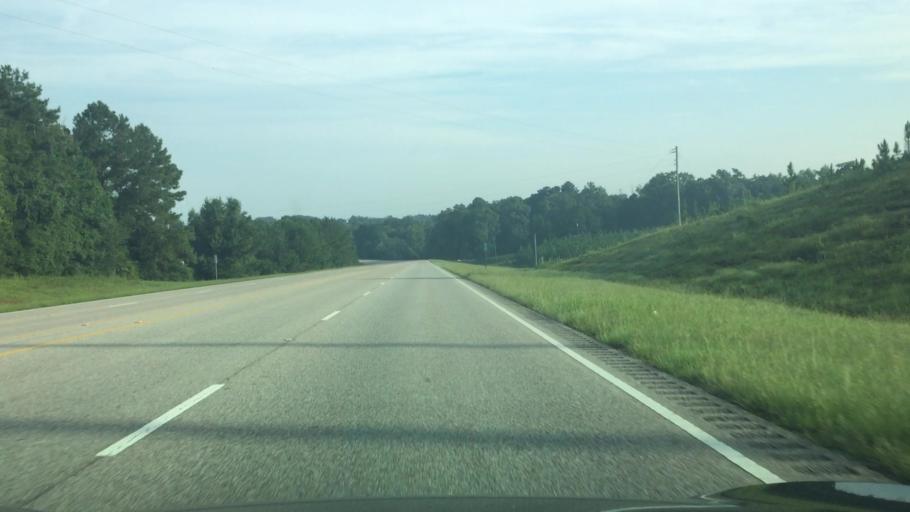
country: US
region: Alabama
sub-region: Covington County
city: Andalusia
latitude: 31.3910
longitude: -86.5722
